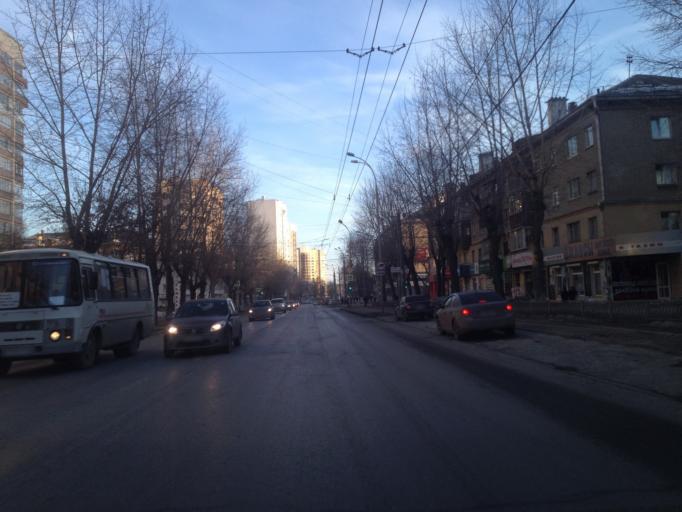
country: RU
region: Sverdlovsk
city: Yekaterinburg
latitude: 56.8041
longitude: 60.6266
